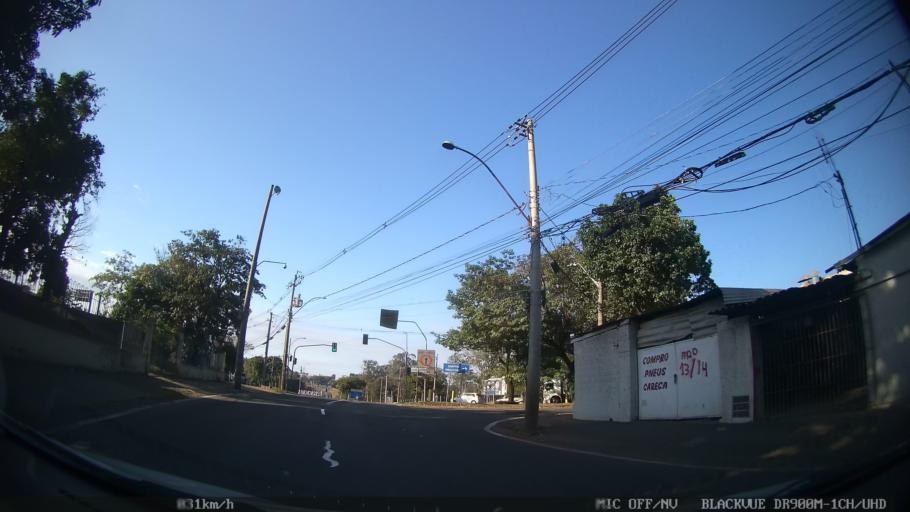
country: BR
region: Sao Paulo
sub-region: Piracicaba
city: Piracicaba
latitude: -22.6990
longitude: -47.6539
